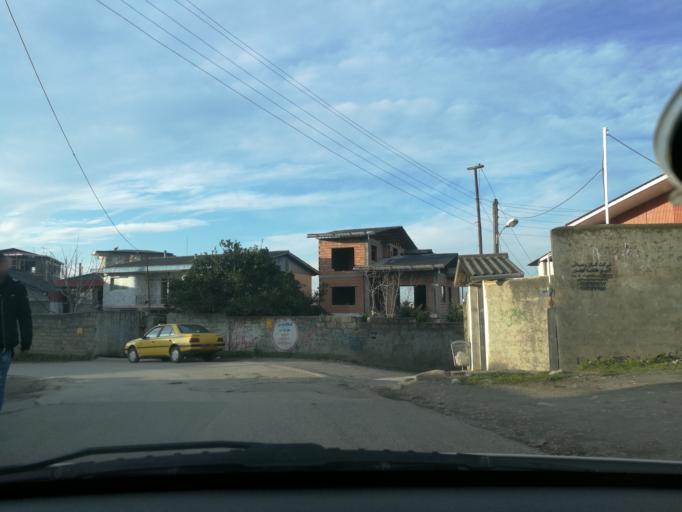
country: IR
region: Mazandaran
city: Chalus
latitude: 36.6400
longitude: 51.4430
